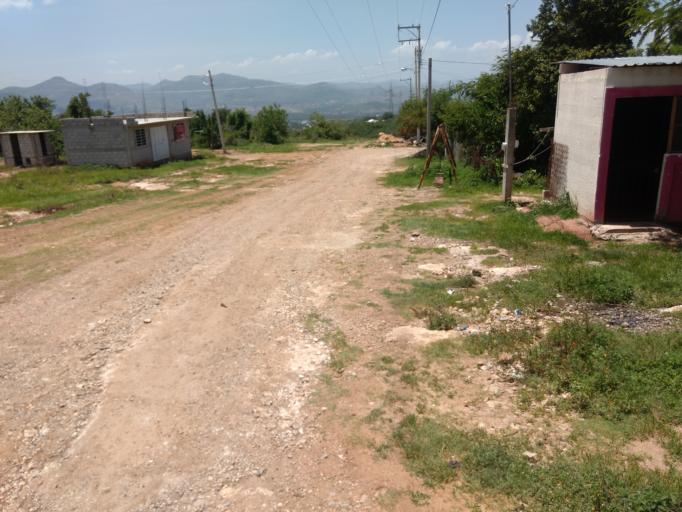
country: MX
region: Oaxaca
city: San Jeronimo Silacayoapilla
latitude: 17.8178
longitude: -97.8131
